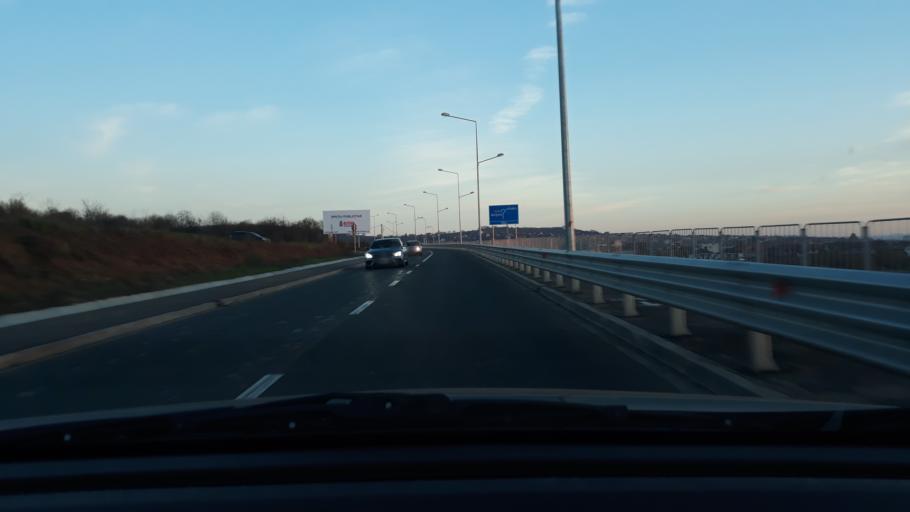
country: RO
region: Bihor
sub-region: Comuna Biharea
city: Oradea
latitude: 47.0979
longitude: 21.9198
